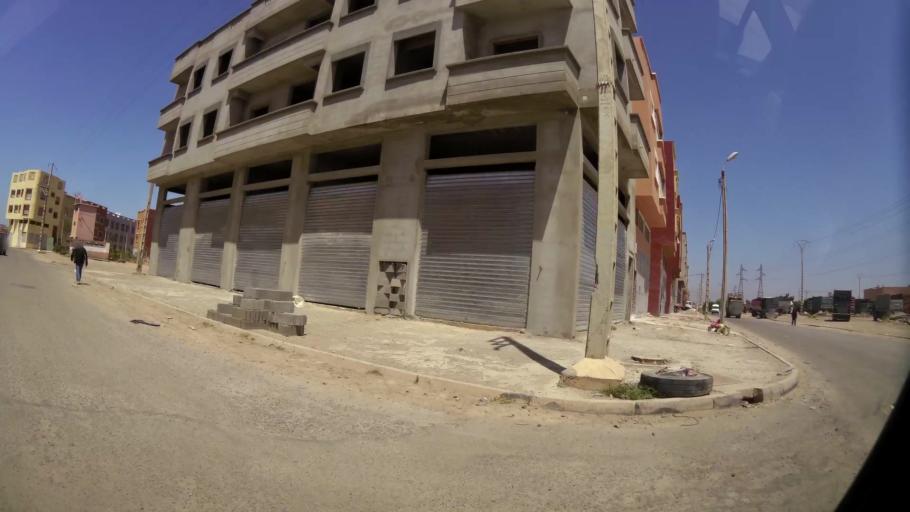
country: MA
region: Souss-Massa-Draa
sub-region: Inezgane-Ait Mellou
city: Inezgane
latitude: 30.3356
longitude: -9.4954
